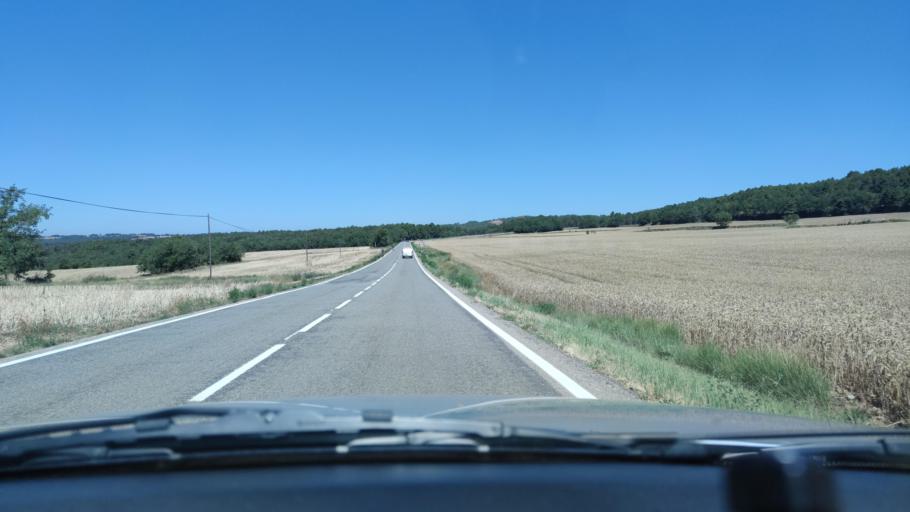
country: ES
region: Catalonia
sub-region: Provincia de Lleida
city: Solsona
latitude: 41.8973
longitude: 1.5407
